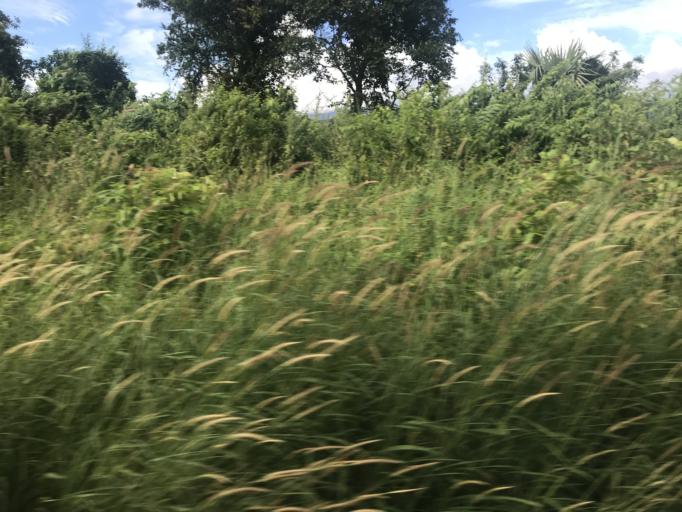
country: IN
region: Kerala
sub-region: Palakkad district
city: Palakkad
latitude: 10.8159
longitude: 76.6836
